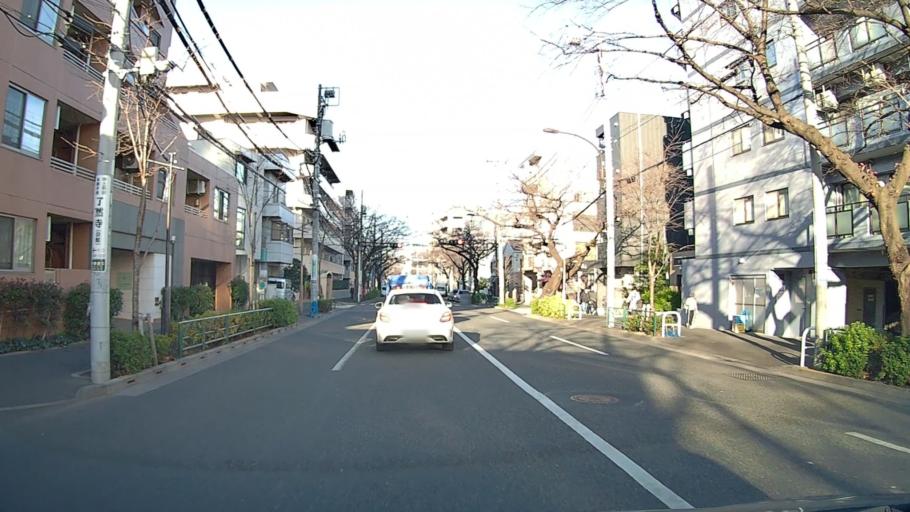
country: JP
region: Tokyo
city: Tokyo
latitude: 35.7178
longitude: 139.6694
